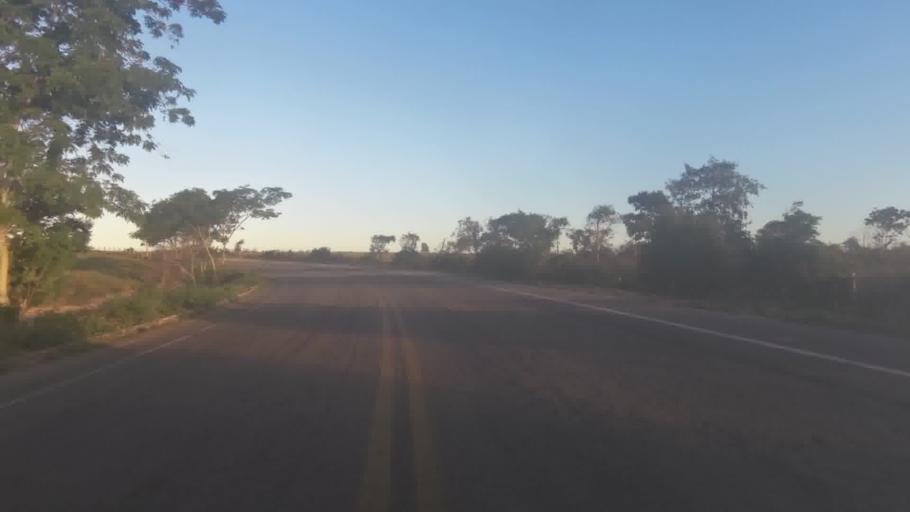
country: BR
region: Espirito Santo
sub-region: Marataizes
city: Marataizes
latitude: -21.1957
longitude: -40.9726
